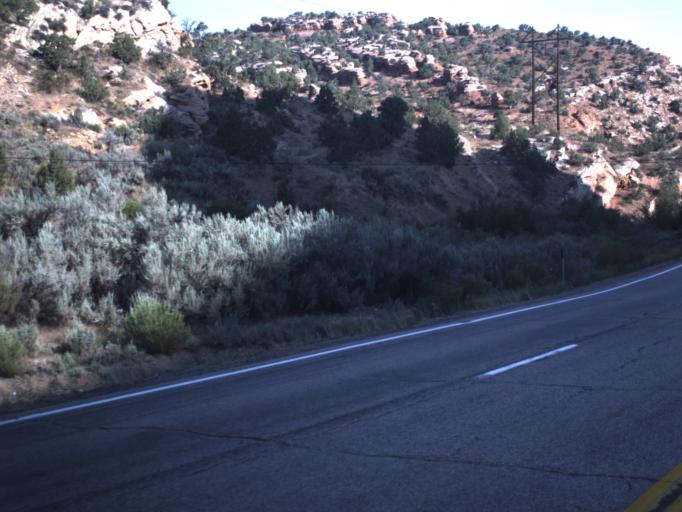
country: US
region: Utah
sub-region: Uintah County
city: Vernal
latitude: 40.5858
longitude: -109.4688
